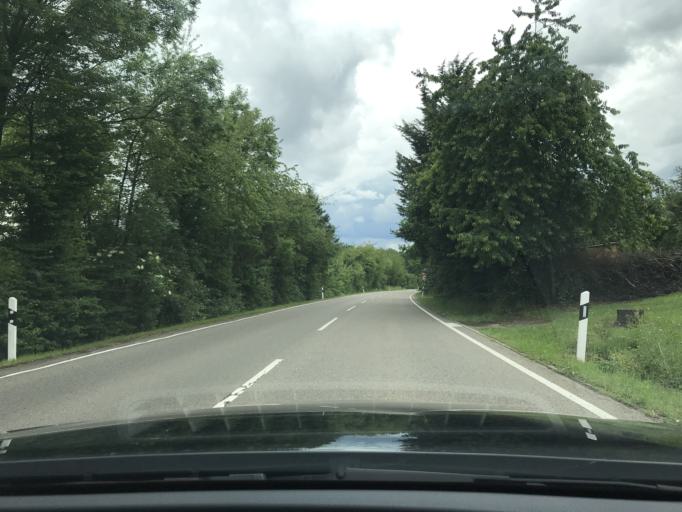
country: DE
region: Baden-Wuerttemberg
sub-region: Regierungsbezirk Stuttgart
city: Waiblingen
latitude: 48.8412
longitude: 9.3373
